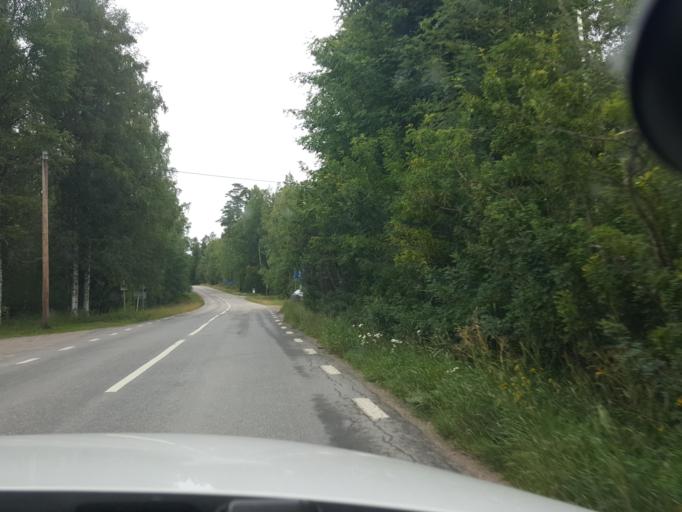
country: SE
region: Gaevleborg
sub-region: Hudiksvalls Kommun
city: Delsbo
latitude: 61.9723
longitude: 16.4663
